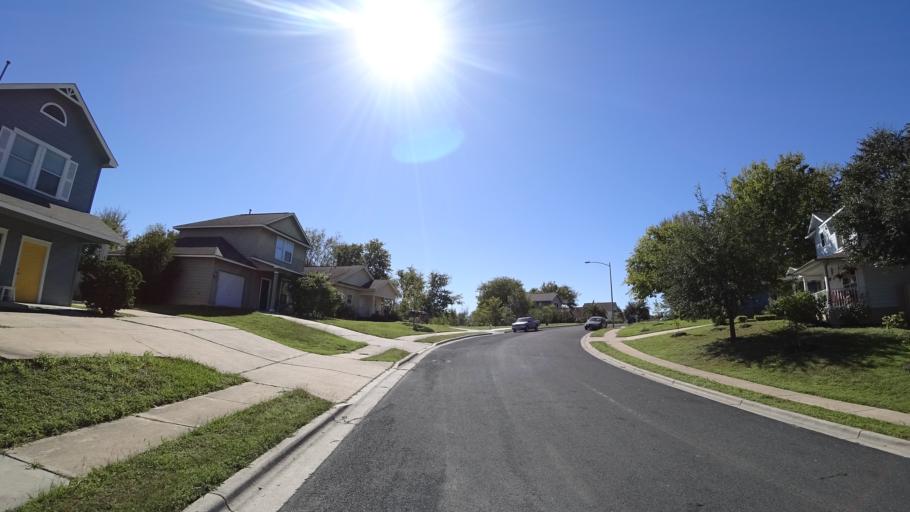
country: US
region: Texas
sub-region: Travis County
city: Hornsby Bend
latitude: 30.2895
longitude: -97.6584
